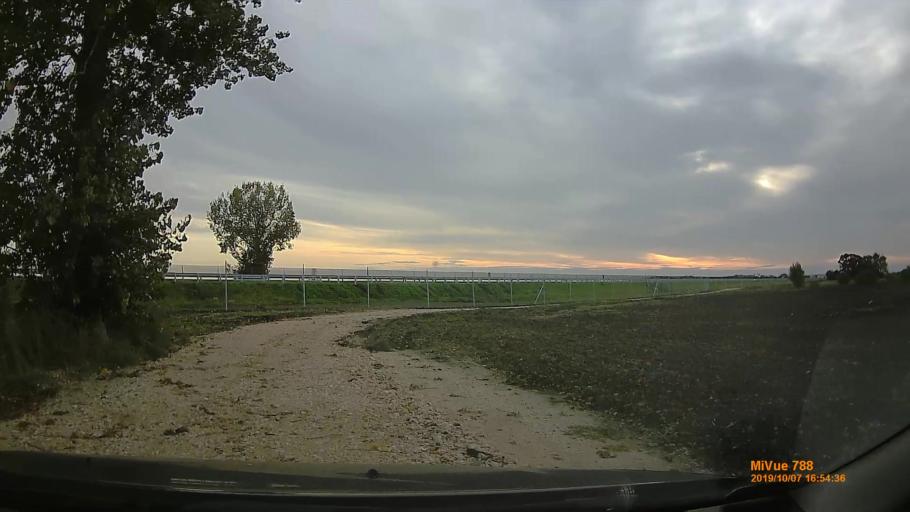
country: HU
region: Bekes
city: Szarvas
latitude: 46.8199
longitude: 20.5775
